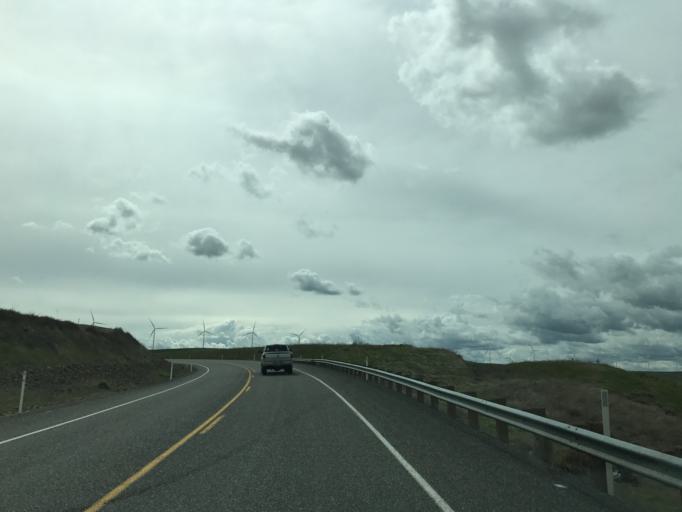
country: US
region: Washington
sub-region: Garfield County
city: Pomeroy
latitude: 46.5751
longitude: -117.7787
